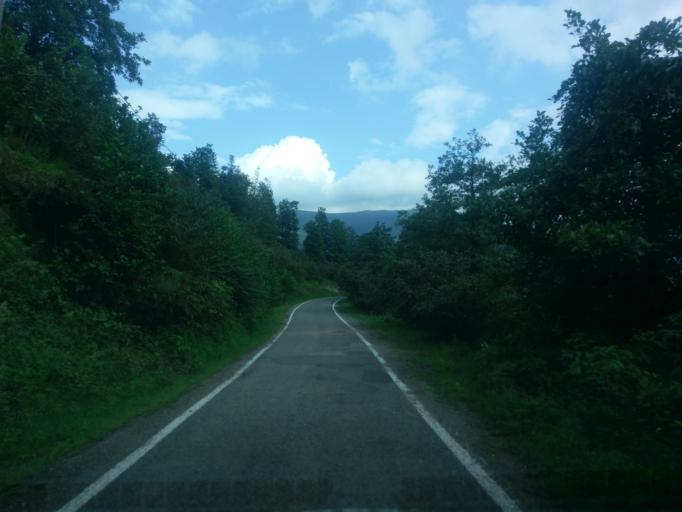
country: TR
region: Ordu
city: Camas
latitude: 40.9259
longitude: 37.6077
